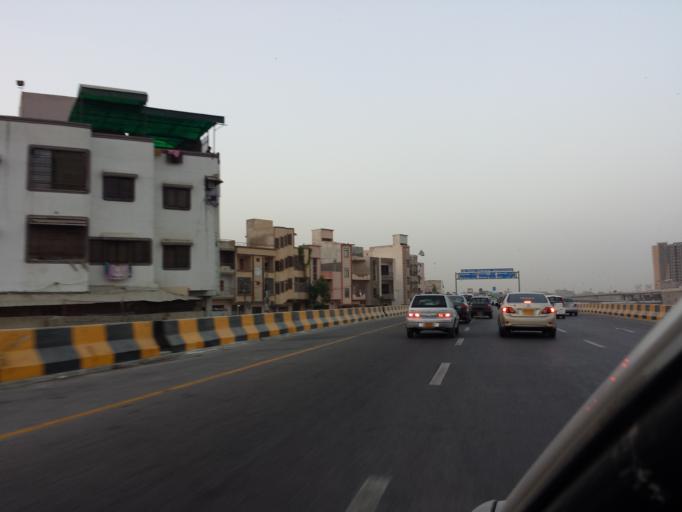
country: PK
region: Sindh
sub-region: Karachi District
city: Karachi
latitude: 24.9027
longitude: 67.0619
